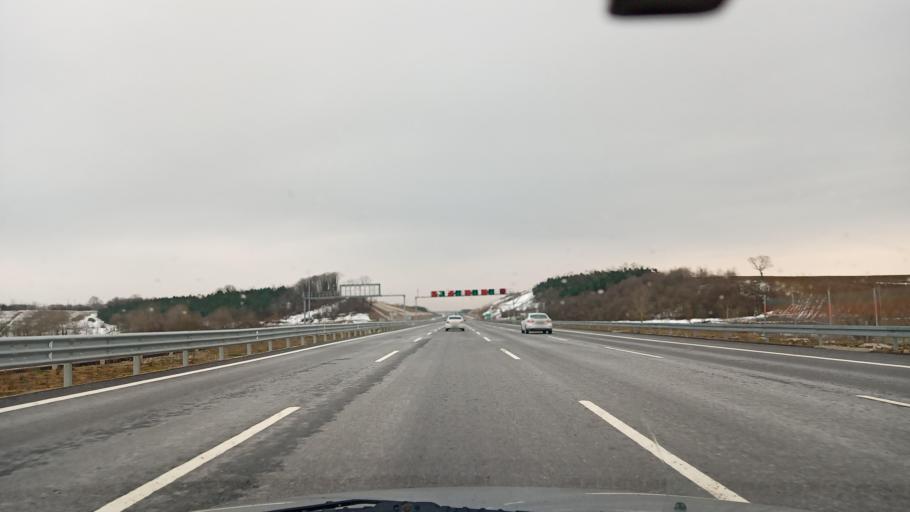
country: TR
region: Kocaeli
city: Akmese
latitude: 40.8464
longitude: 30.2479
